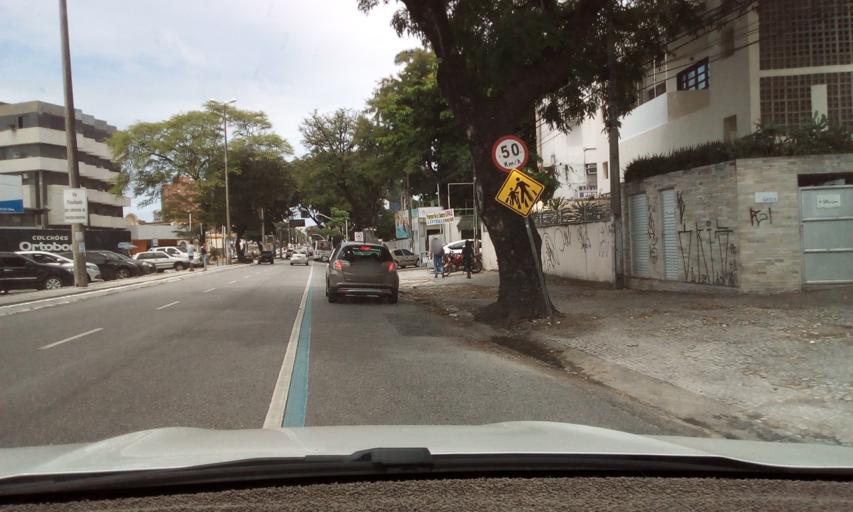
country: BR
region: Paraiba
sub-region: Joao Pessoa
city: Joao Pessoa
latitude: -7.1199
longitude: -34.8695
